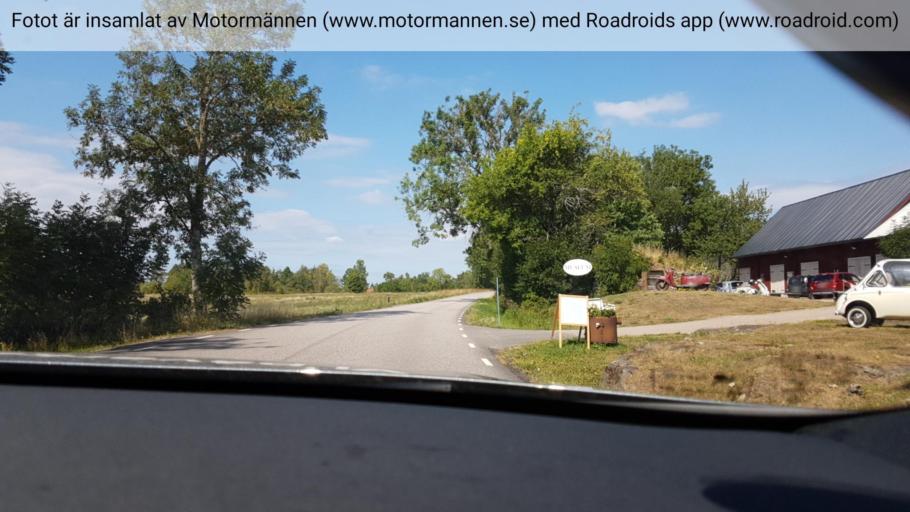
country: SE
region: Vaestra Goetaland
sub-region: Gotene Kommun
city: Kallby
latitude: 58.5329
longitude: 13.3229
